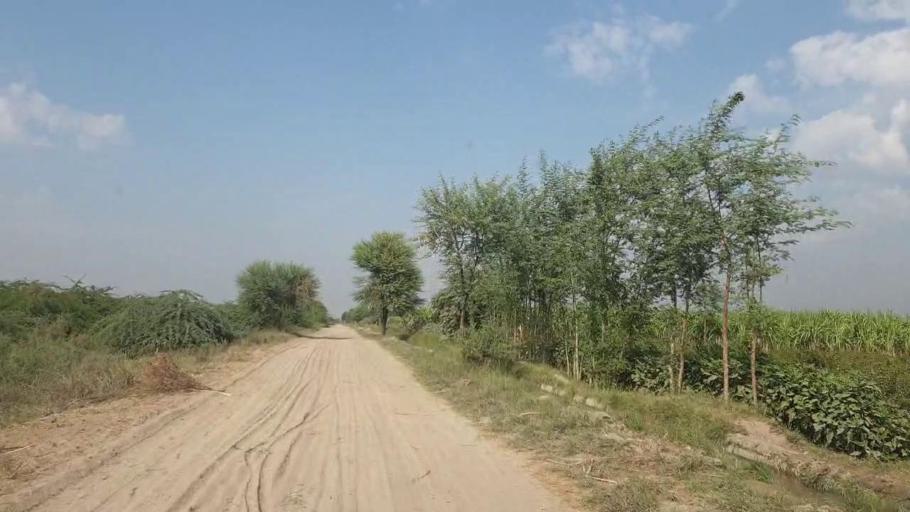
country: PK
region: Sindh
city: Digri
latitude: 25.0264
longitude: 69.0710
